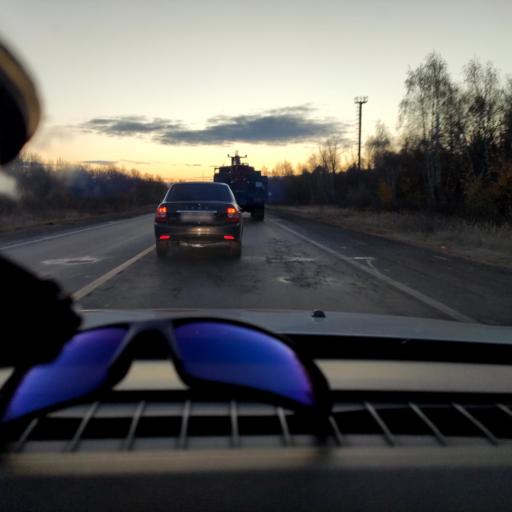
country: RU
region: Samara
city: Chapayevsk
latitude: 52.9929
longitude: 49.8284
